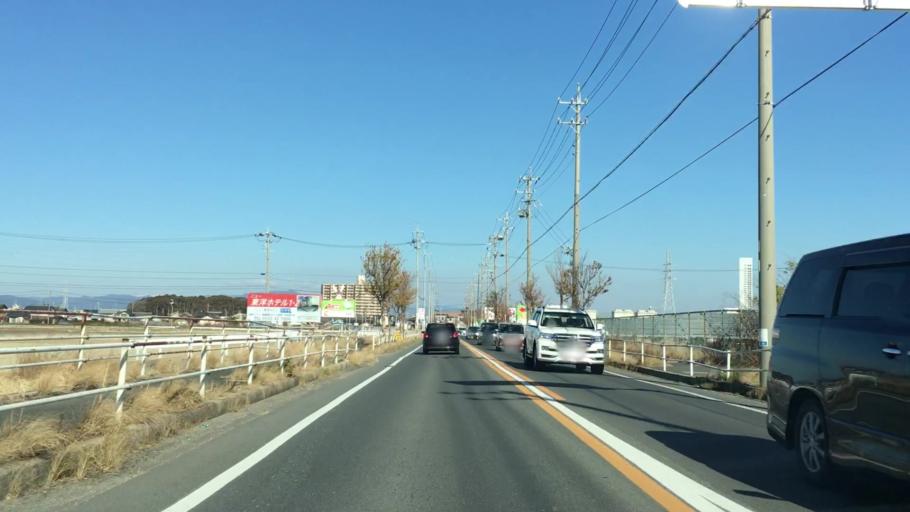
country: JP
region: Aichi
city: Toyohashi
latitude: 34.7347
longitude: 137.3610
